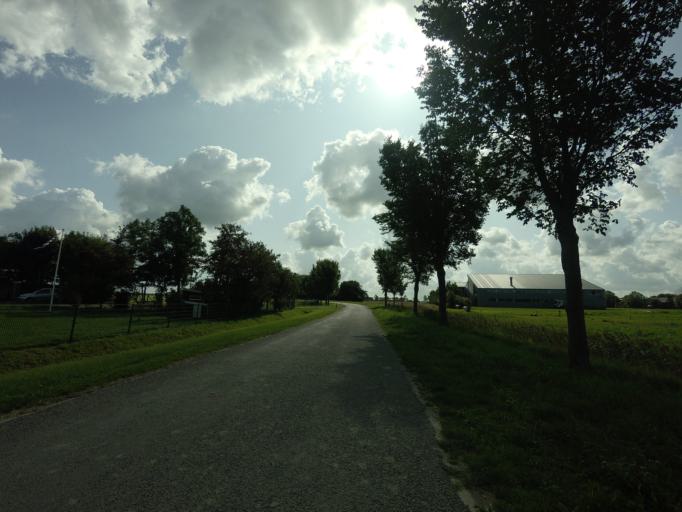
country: NL
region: Friesland
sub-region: Gemeente Het Bildt
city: Minnertsga
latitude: 53.2584
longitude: 5.6008
